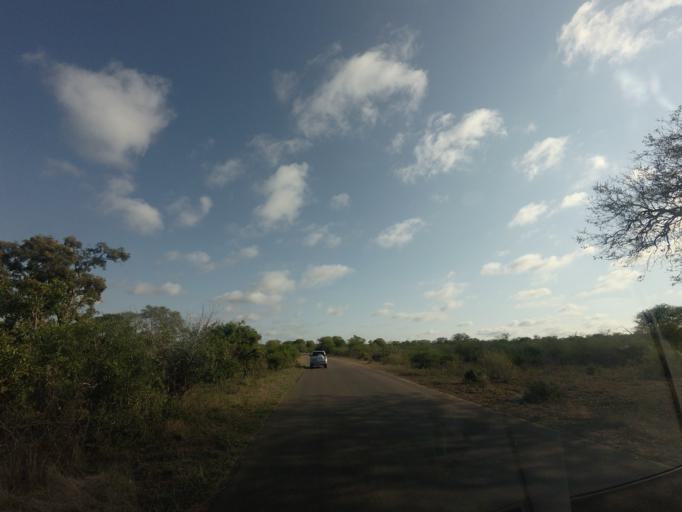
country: ZA
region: Mpumalanga
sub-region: Ehlanzeni District
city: Komatipoort
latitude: -25.2599
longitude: 31.8467
